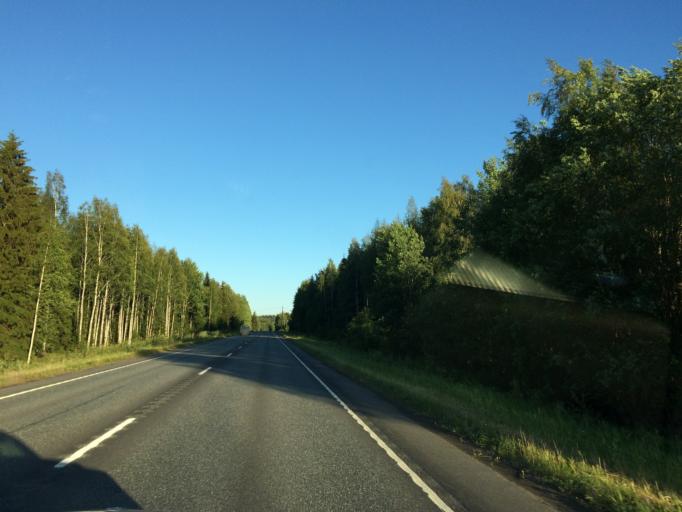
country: FI
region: Haeme
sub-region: Haemeenlinna
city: Tervakoski
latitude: 60.7789
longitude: 24.6923
